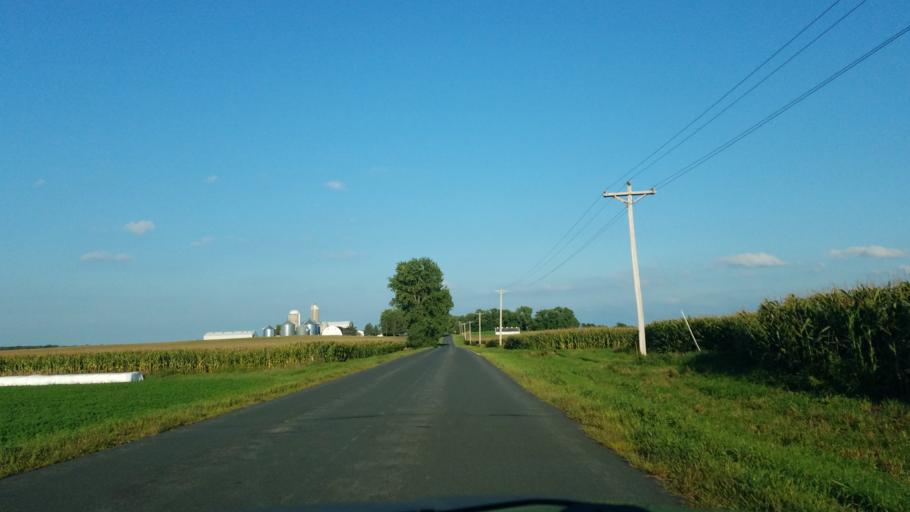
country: US
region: Wisconsin
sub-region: Saint Croix County
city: Roberts
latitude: 45.0070
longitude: -92.5486
